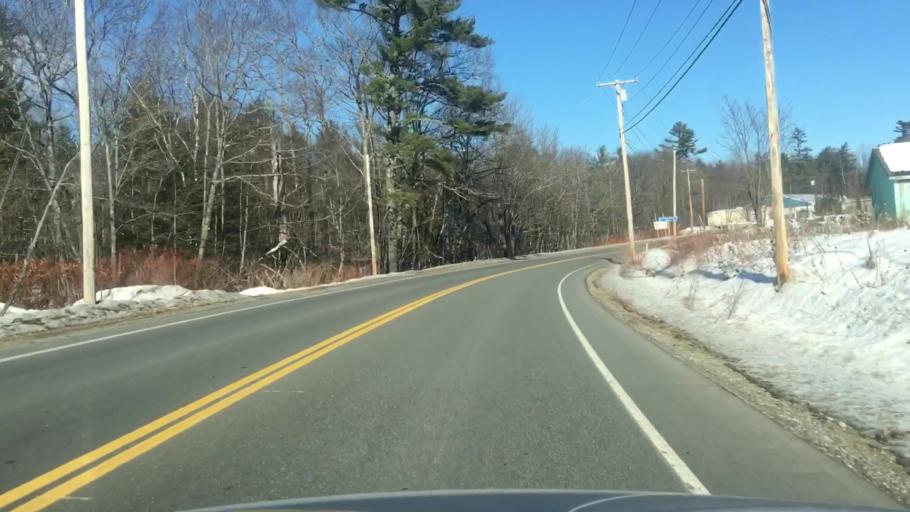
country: US
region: Maine
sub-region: Somerset County
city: Madison
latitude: 44.9465
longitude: -69.8647
